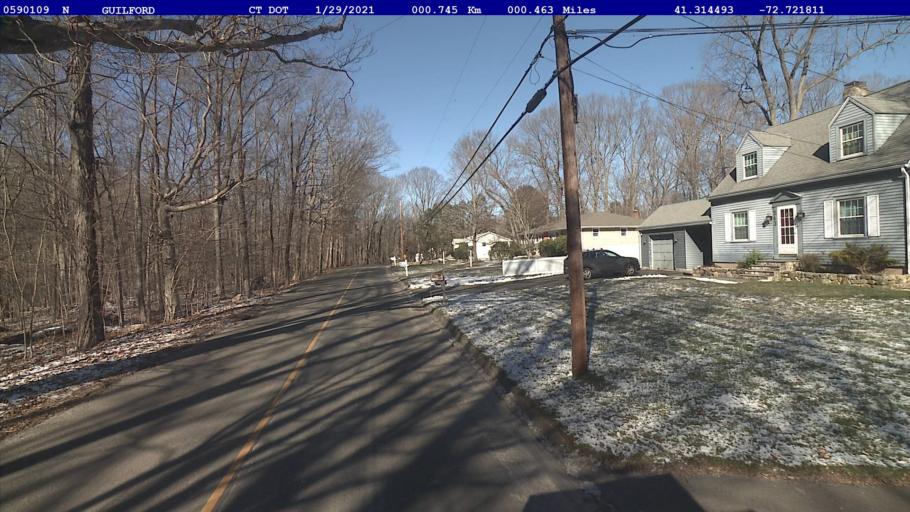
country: US
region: Connecticut
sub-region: New Haven County
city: North Branford
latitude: 41.3145
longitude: -72.7218
